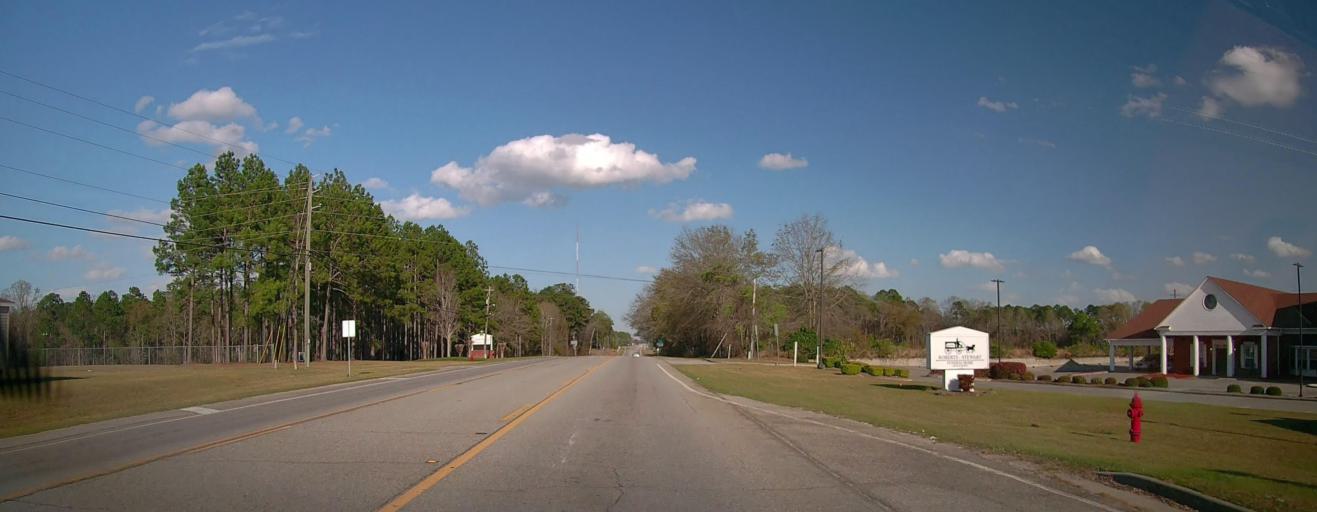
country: US
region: Georgia
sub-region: Toombs County
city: Vidalia
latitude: 32.2180
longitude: -82.4425
